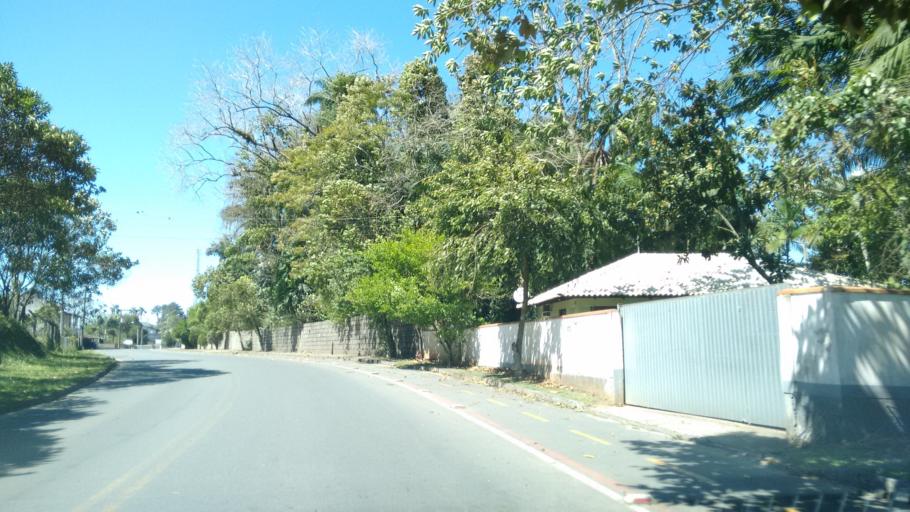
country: BR
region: Santa Catarina
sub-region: Blumenau
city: Blumenau
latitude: -26.8888
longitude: -49.1309
